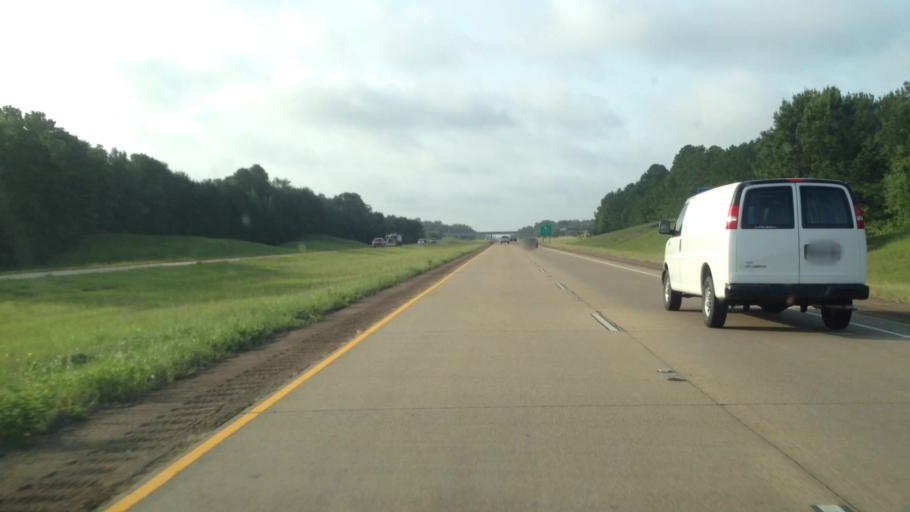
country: US
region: Louisiana
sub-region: Rapides Parish
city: Lecompte
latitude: 31.0794
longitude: -92.4381
